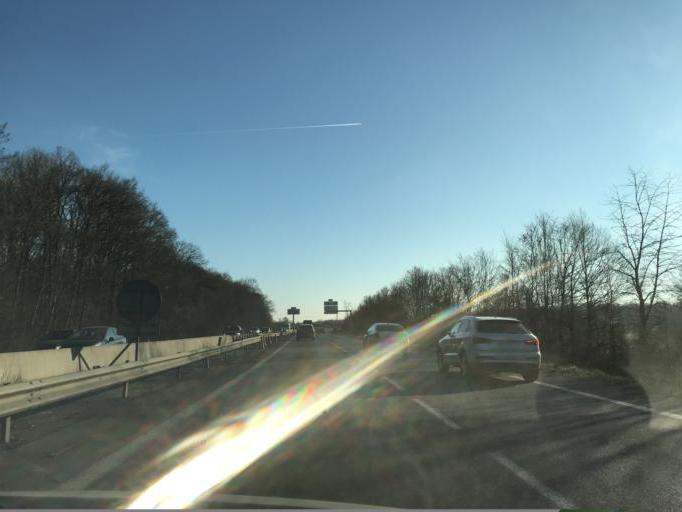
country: FR
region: Ile-de-France
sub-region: Departement de Seine-et-Marne
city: Lesigny
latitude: 48.7549
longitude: 2.6150
